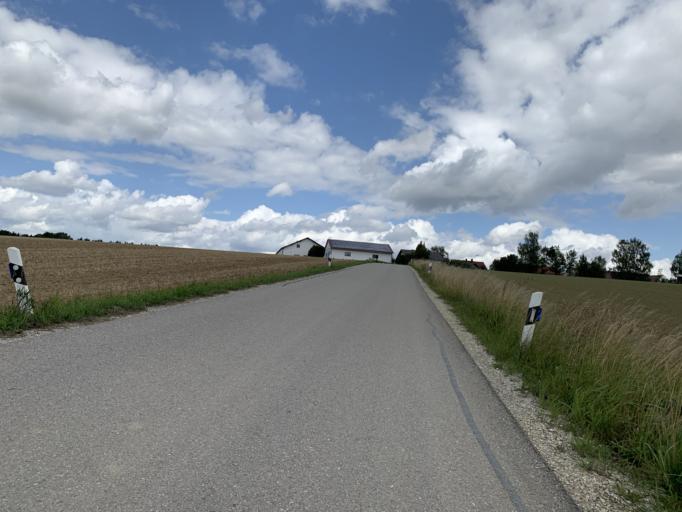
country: DE
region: Bavaria
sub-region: Upper Bavaria
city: Zolling
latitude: 48.4320
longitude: 11.7738
